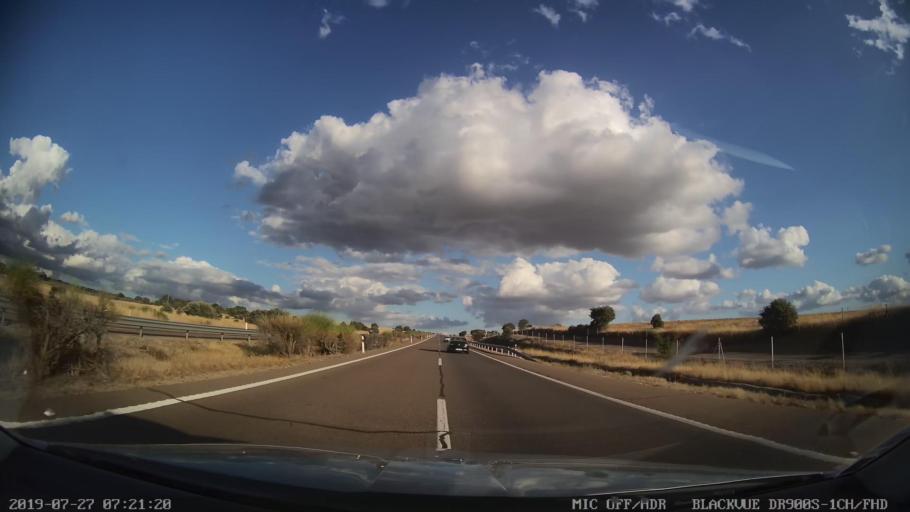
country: ES
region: Extremadura
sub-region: Provincia de Caceres
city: Santa Cruz de la Sierra
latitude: 39.3642
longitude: -5.8708
